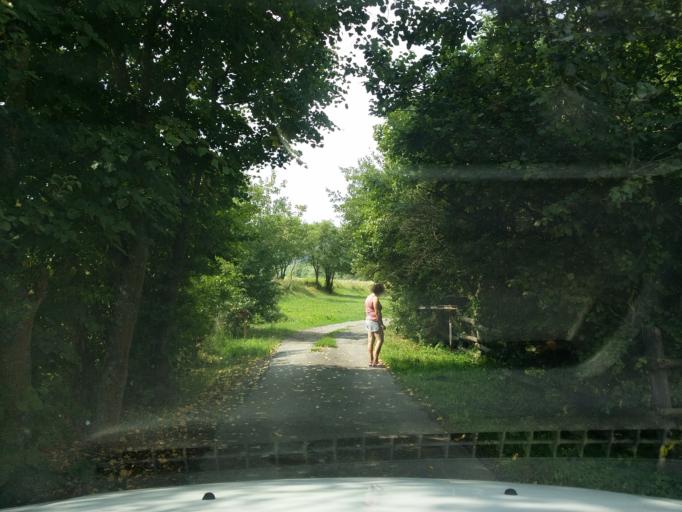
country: HU
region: Borsod-Abauj-Zemplen
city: Sarospatak
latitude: 48.4480
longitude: 21.5271
